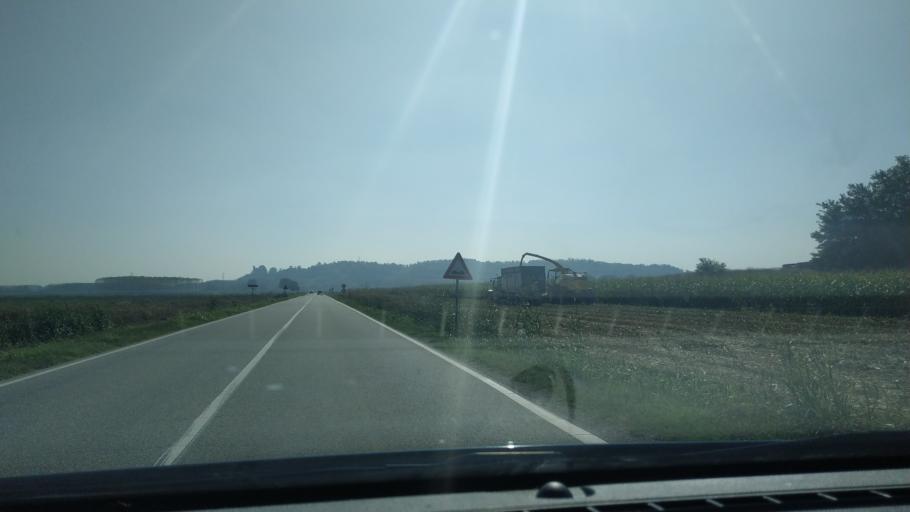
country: IT
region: Piedmont
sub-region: Provincia di Alessandria
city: Giarole
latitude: 45.0738
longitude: 8.5756
